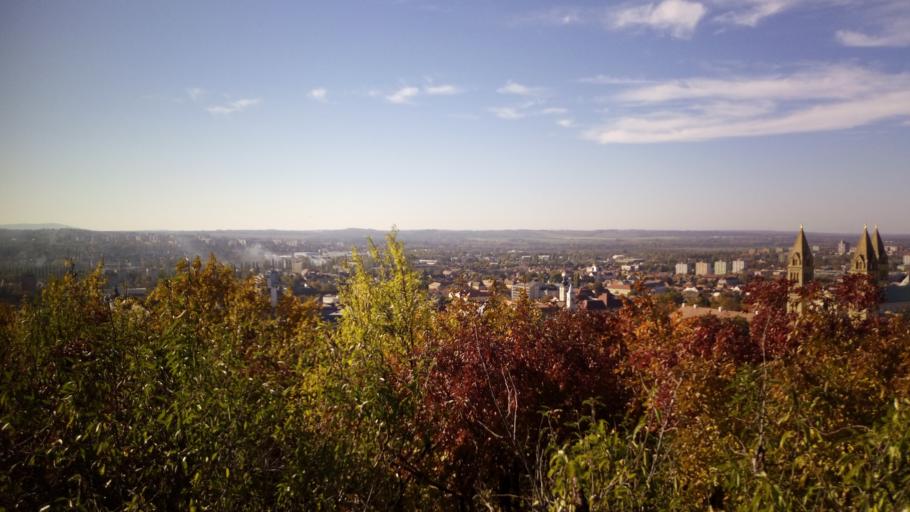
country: HU
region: Baranya
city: Pecs
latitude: 46.0808
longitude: 18.2276
